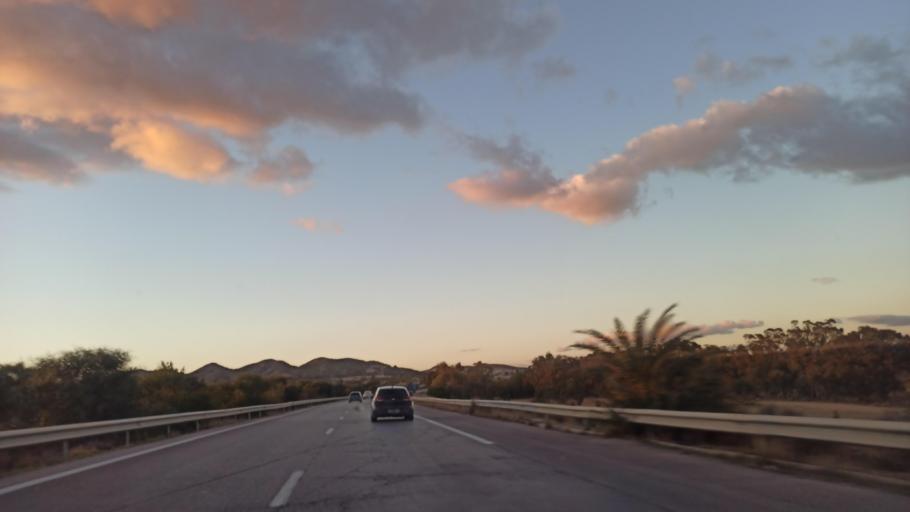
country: TN
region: Susah
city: Harqalah
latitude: 36.2152
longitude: 10.4214
